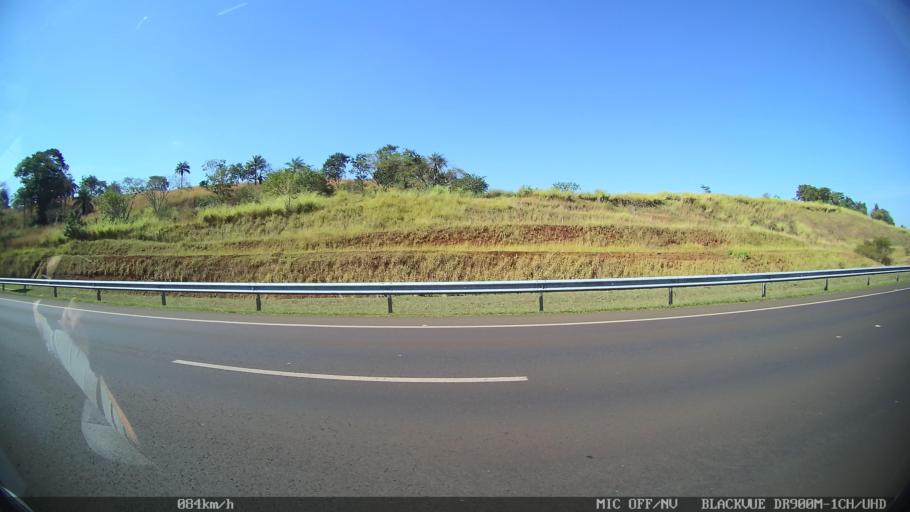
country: BR
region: Sao Paulo
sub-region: Franca
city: Franca
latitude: -20.6088
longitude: -47.4538
